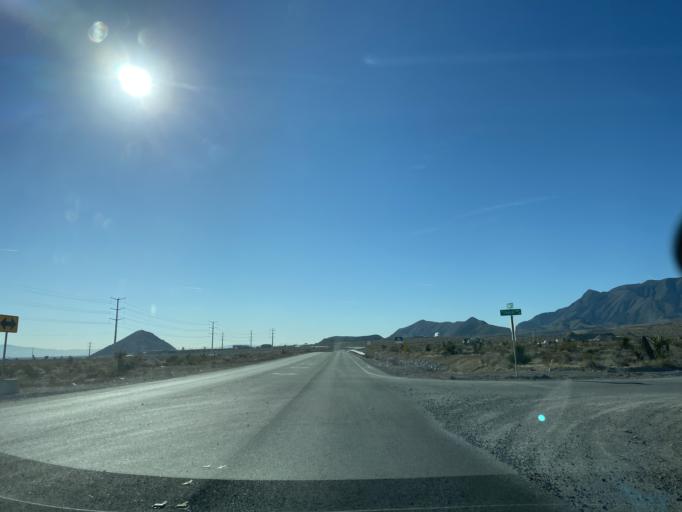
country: US
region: Nevada
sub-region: Clark County
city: Summerlin South
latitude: 36.2701
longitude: -115.3301
